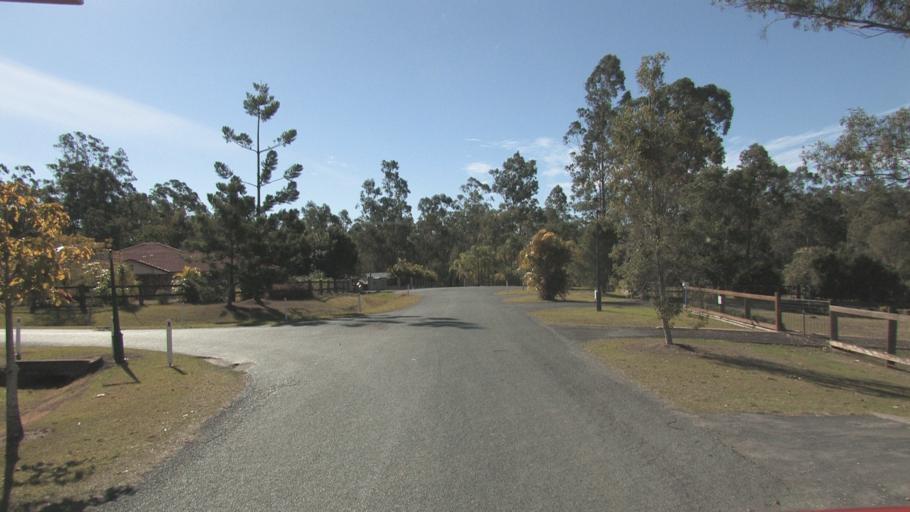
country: AU
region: Queensland
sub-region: Ipswich
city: Springfield Lakes
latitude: -27.7291
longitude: 152.9295
